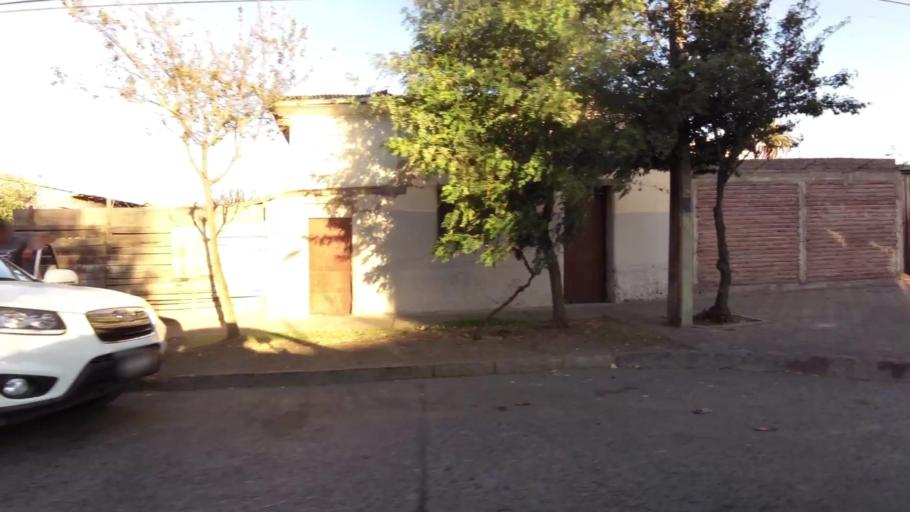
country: CL
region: O'Higgins
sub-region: Provincia de Cachapoal
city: Rancagua
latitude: -34.1726
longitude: -70.7529
